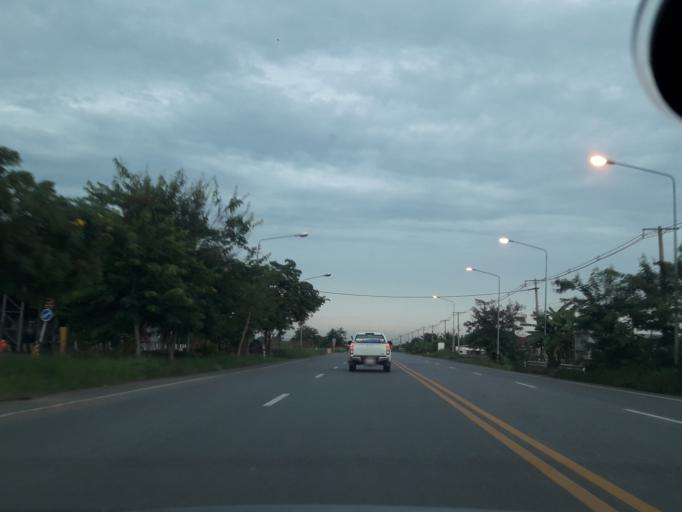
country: TH
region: Pathum Thani
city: Nong Suea
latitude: 14.1144
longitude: 100.7472
